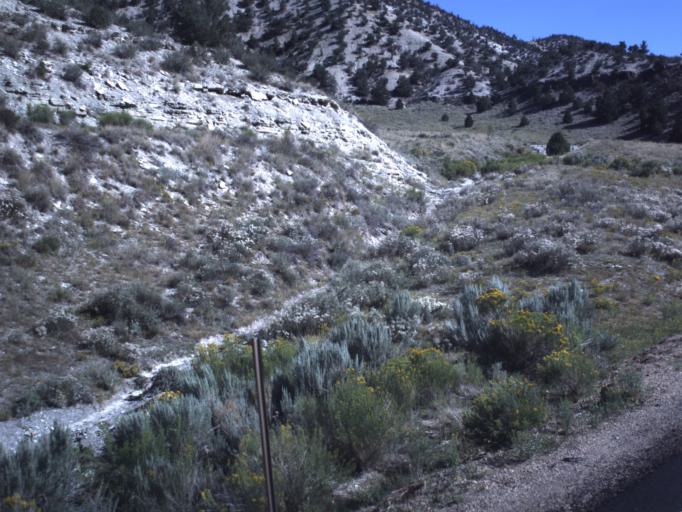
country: US
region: Utah
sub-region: Carbon County
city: Helper
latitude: 39.9394
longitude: -110.6660
